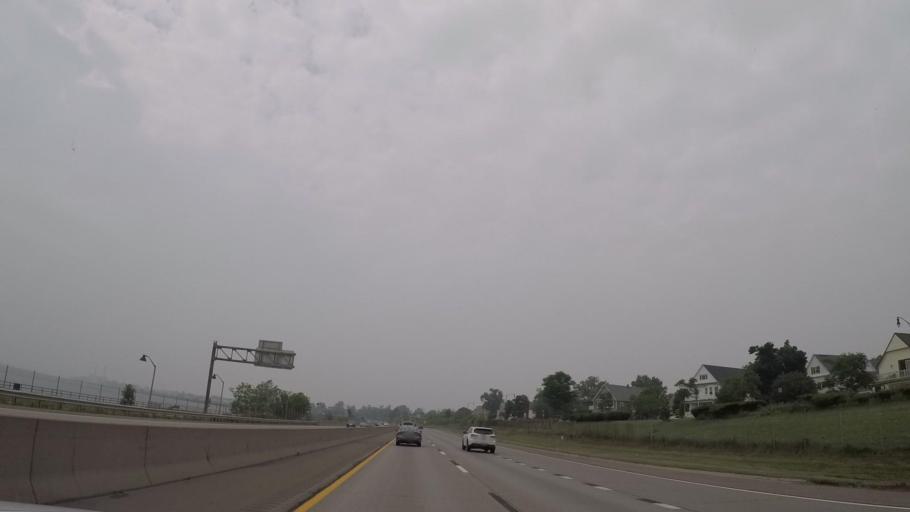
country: US
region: New York
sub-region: Erie County
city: Kenmore
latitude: 42.9488
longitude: -78.9090
